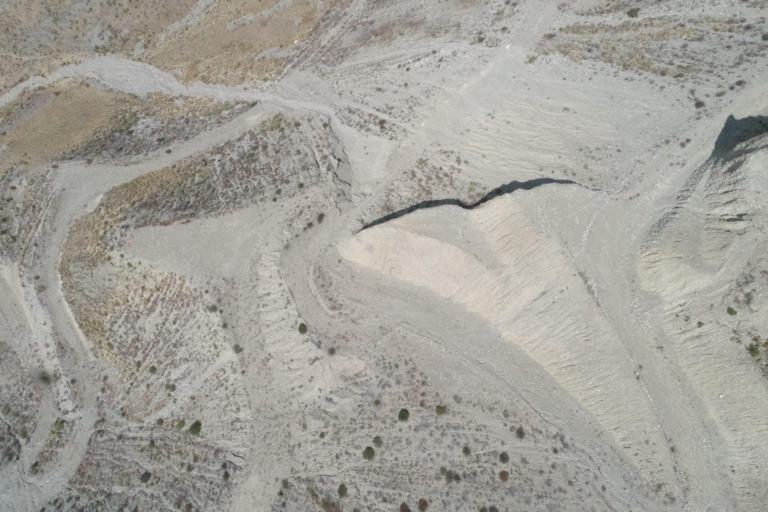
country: BO
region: La Paz
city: La Paz
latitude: -16.4718
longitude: -68.0973
